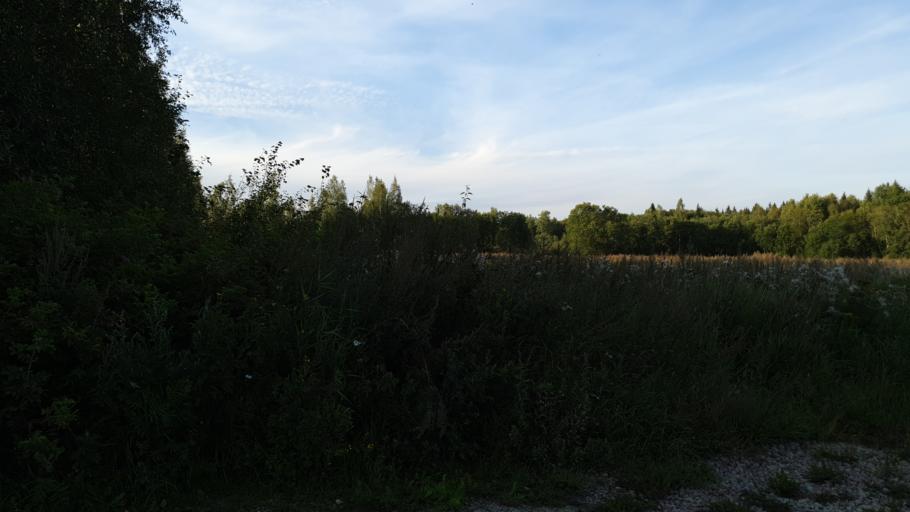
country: RU
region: Leningrad
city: Ivangorod
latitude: 59.4291
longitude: 28.3225
